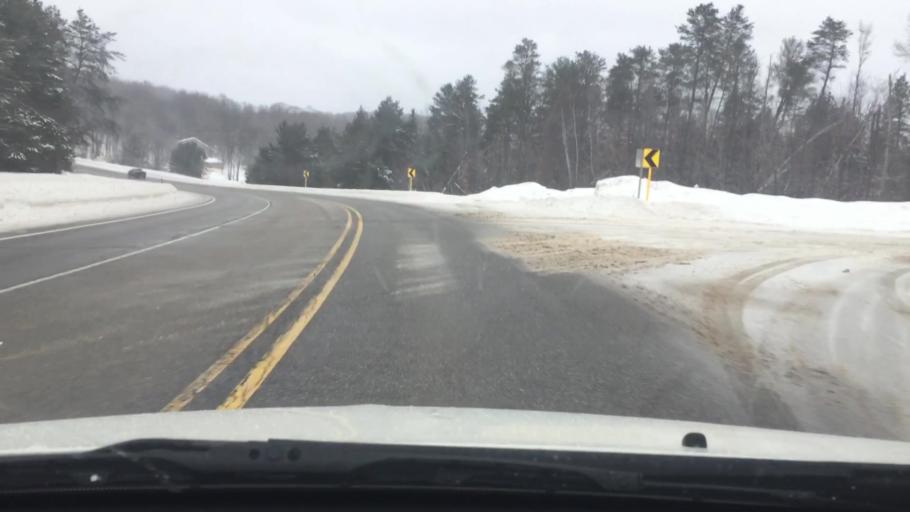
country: US
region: Michigan
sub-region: Otsego County
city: Gaylord
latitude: 45.0597
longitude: -84.7764
